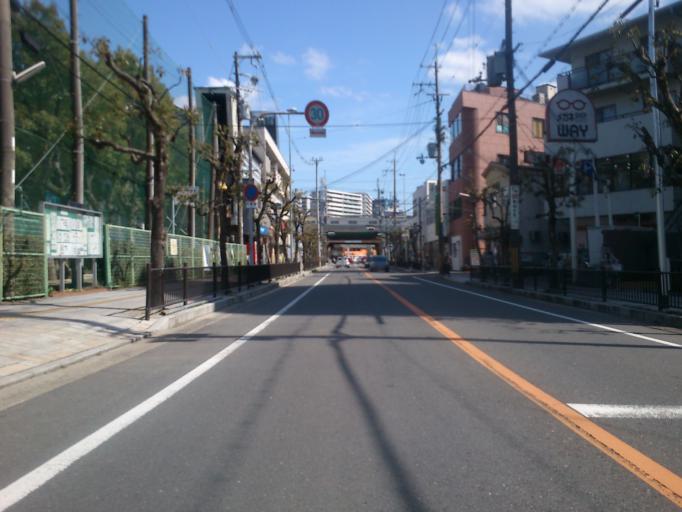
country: JP
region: Kyoto
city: Yawata
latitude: 34.8789
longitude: 135.6666
